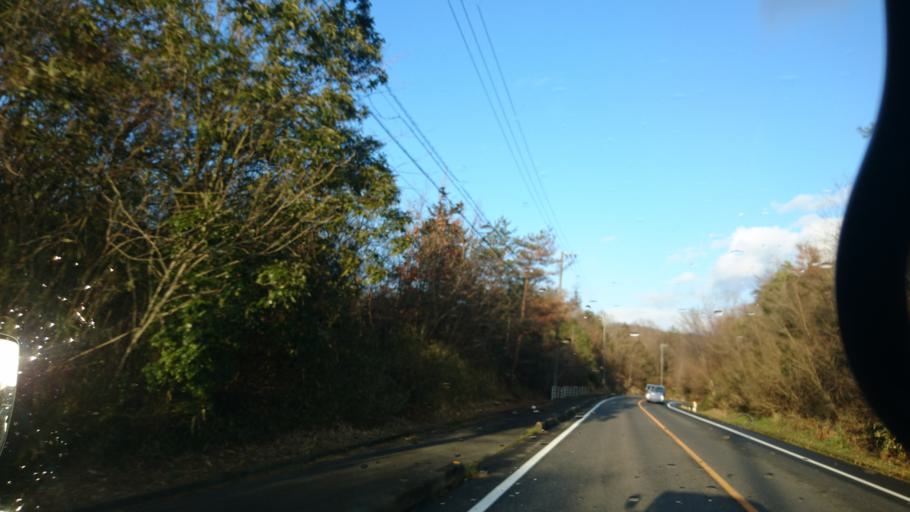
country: JP
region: Mie
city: Ueno-ebisumachi
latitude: 34.7596
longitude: 136.0810
